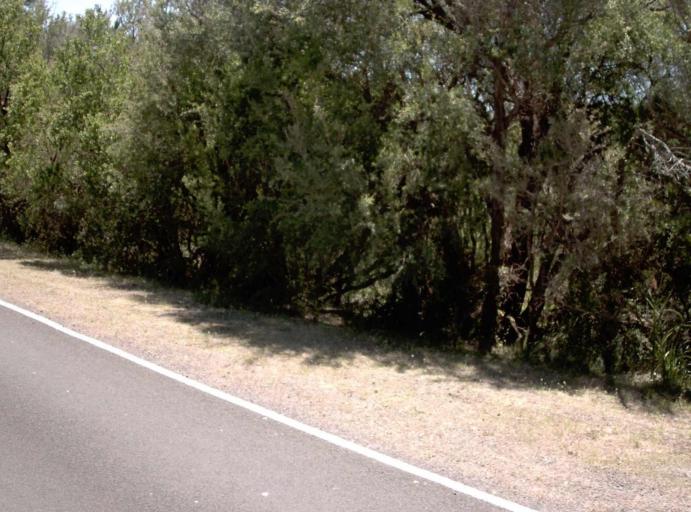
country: AU
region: Victoria
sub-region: Latrobe
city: Morwell
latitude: -38.8602
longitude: 146.2529
